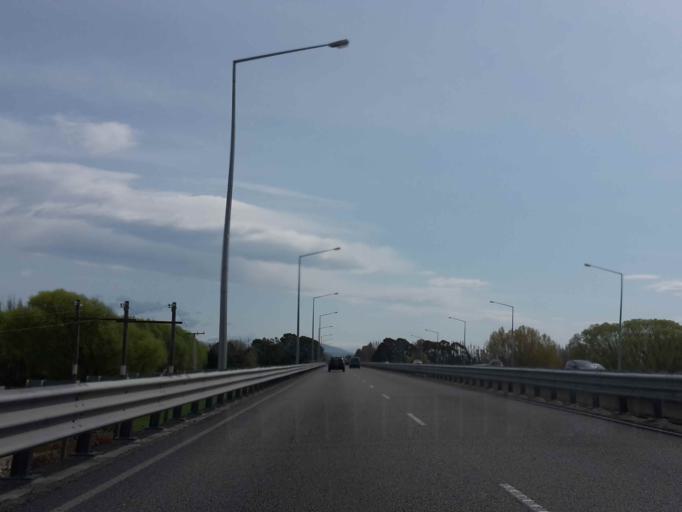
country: NZ
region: Canterbury
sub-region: Waimakariri District
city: Kaiapoi
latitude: -43.4151
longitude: 172.6466
